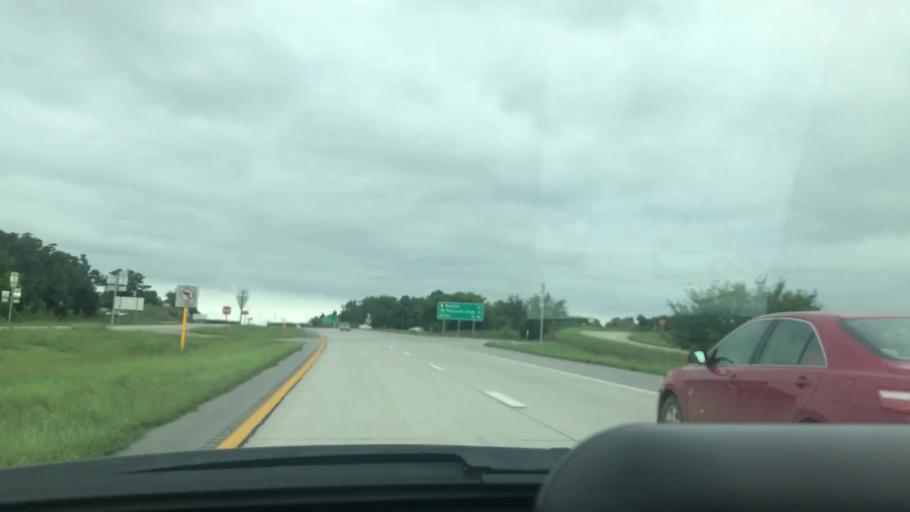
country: US
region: Missouri
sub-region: Greene County
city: Fair Grove
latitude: 37.4572
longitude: -93.1400
